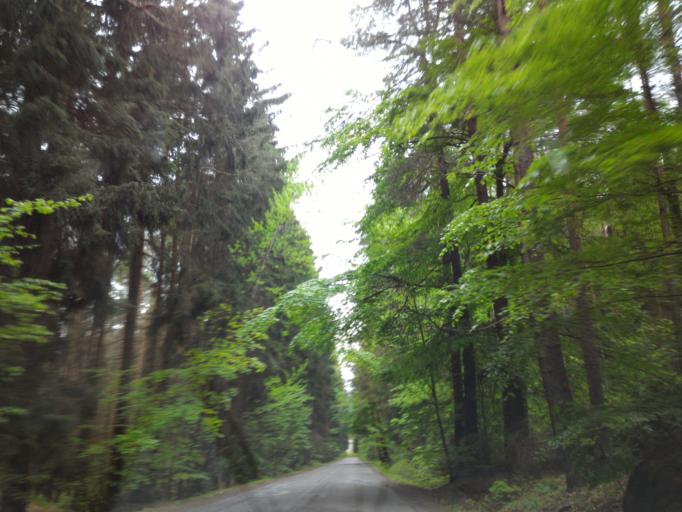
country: CZ
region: Vysocina
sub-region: Okres Havlickuv Brod
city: Svetla nad Sazavou
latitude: 49.6212
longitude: 15.3964
